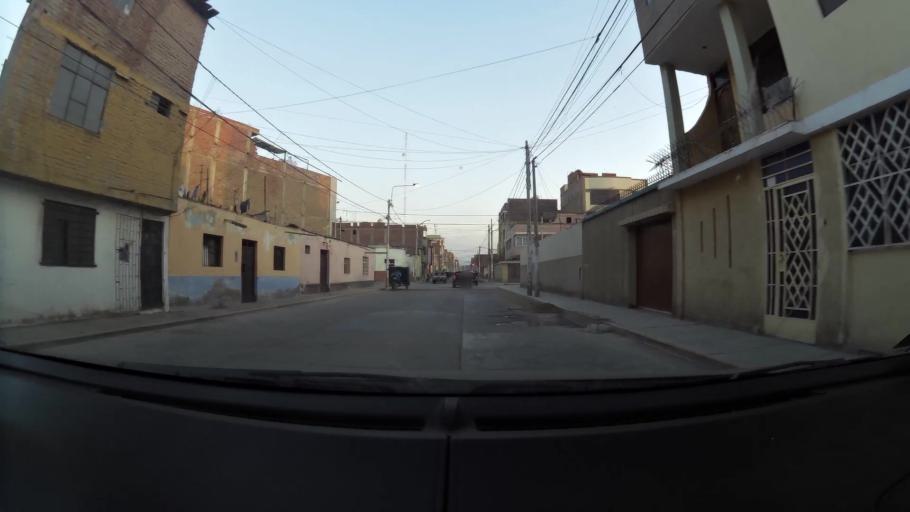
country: PE
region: Lambayeque
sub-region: Provincia de Chiclayo
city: Santa Rosa
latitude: -6.7659
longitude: -79.8316
